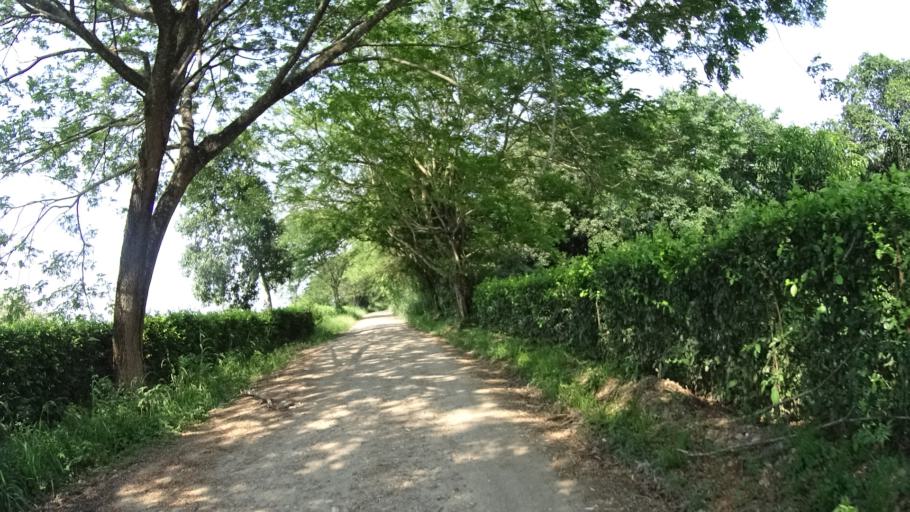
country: CO
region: Cundinamarca
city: Puerto Salgar
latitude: 5.5379
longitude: -74.6799
